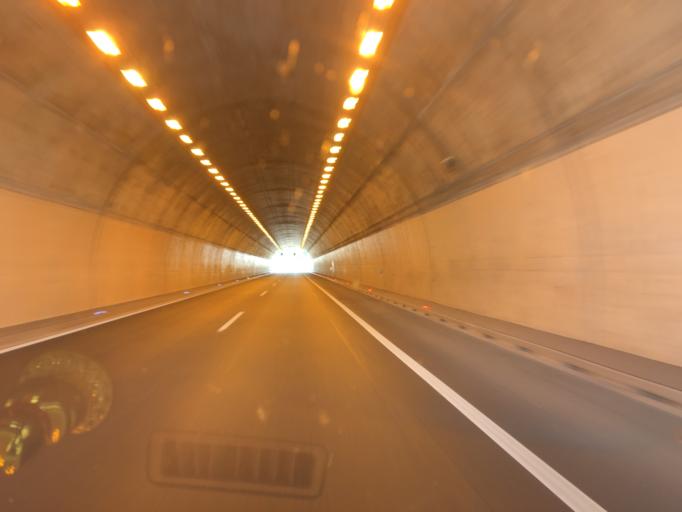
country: SI
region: Maribor
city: Maribor
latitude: 46.5573
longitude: 15.6884
